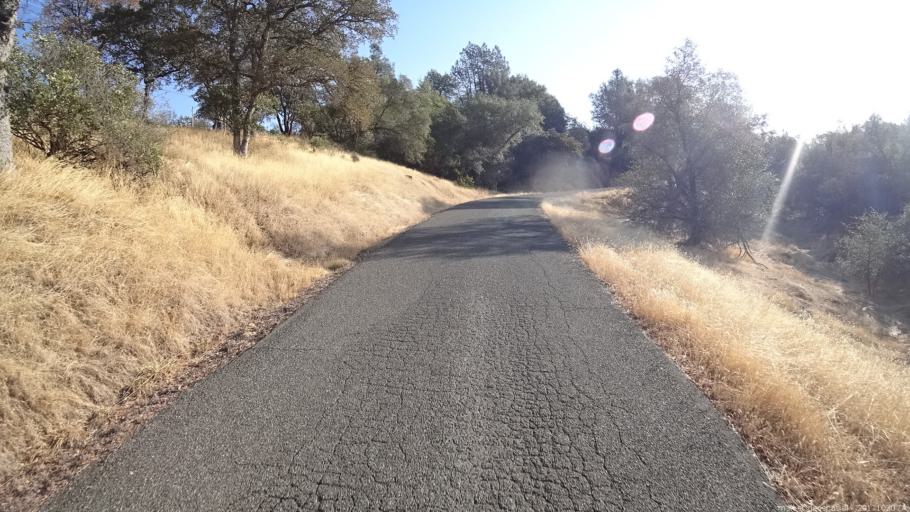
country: US
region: California
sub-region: Shasta County
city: Palo Cedro
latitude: 40.5676
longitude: -122.1391
